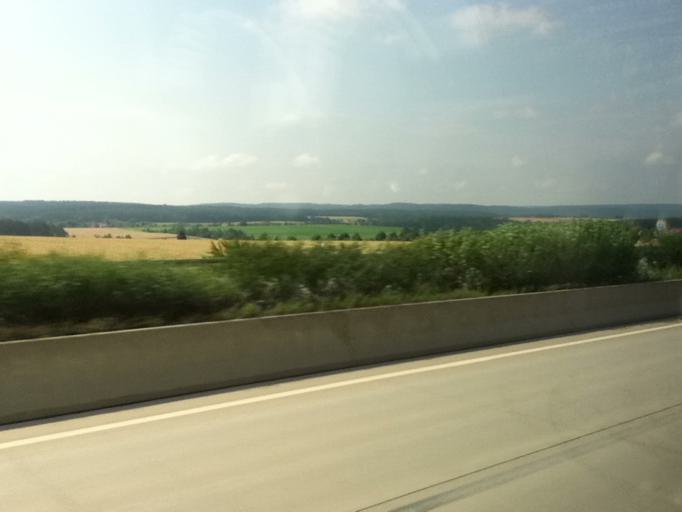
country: DE
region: Thuringia
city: Quirla
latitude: 50.8692
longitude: 11.7793
